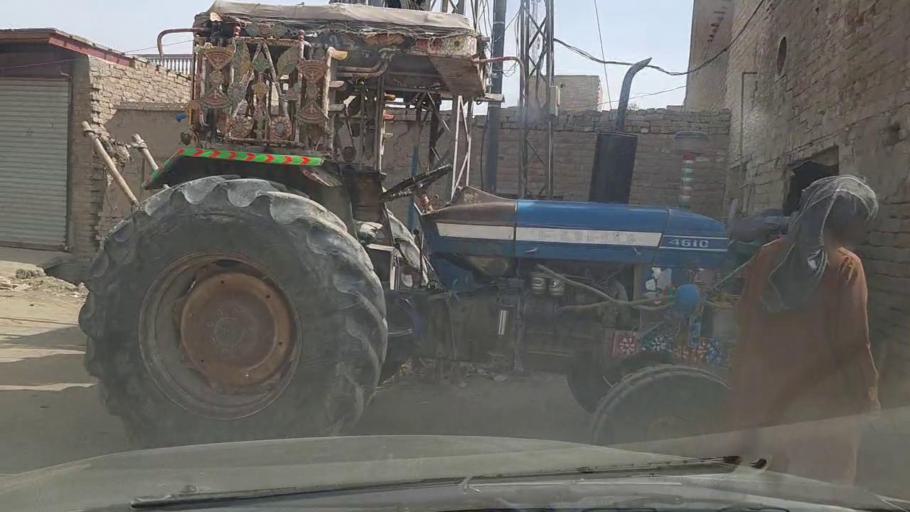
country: PK
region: Sindh
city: Chak
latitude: 27.8292
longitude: 68.7759
